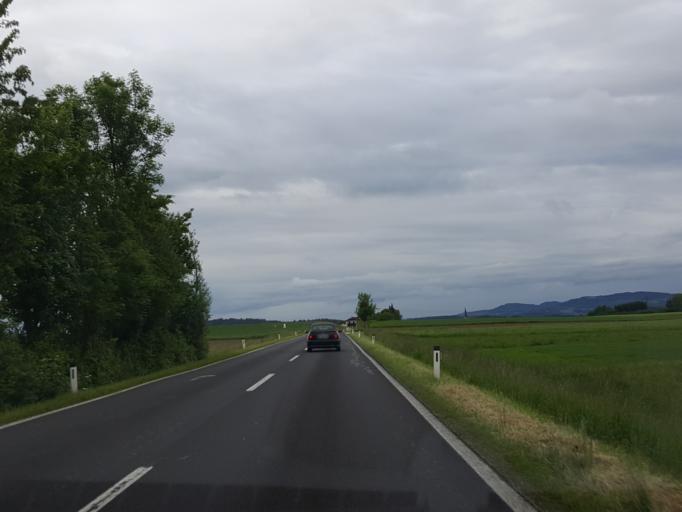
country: AT
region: Upper Austria
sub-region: Politischer Bezirk Vocklabruck
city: Gampern
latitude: 47.9711
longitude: 13.5652
